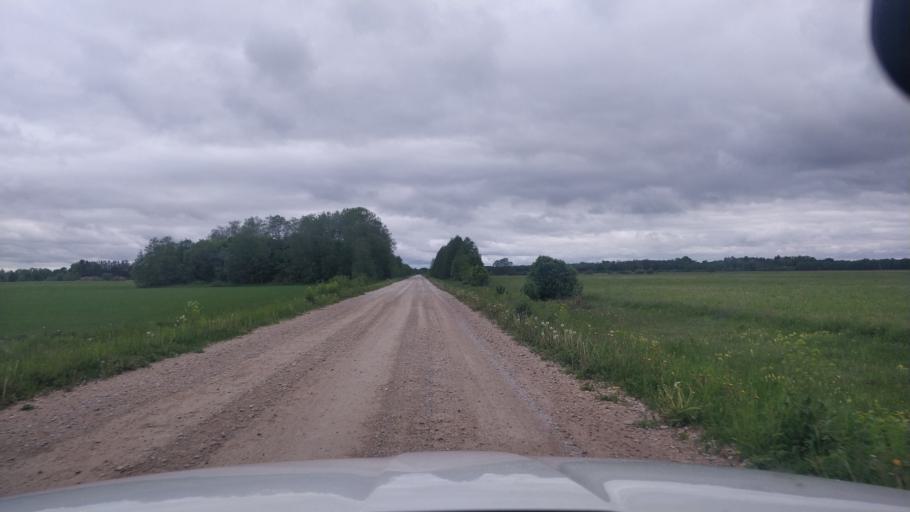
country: EE
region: Raplamaa
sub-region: Maerjamaa vald
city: Marjamaa
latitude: 58.7476
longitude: 24.1947
